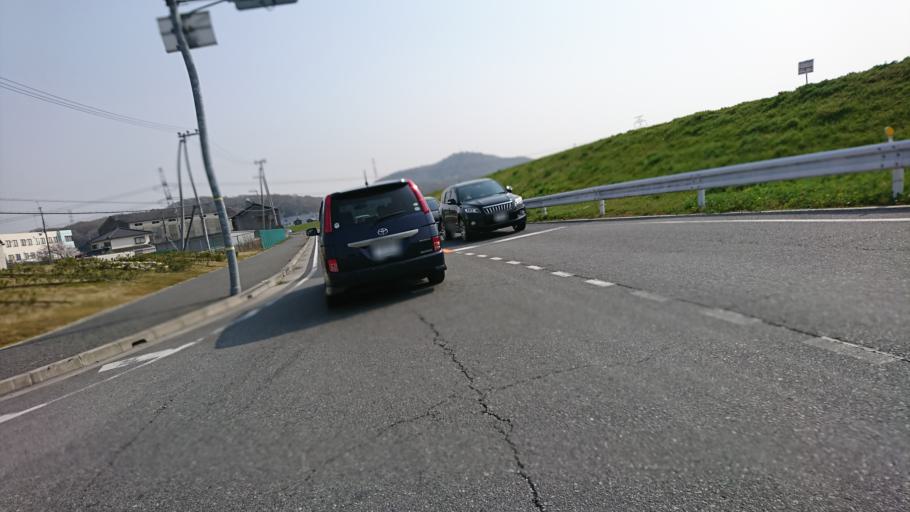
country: JP
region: Hyogo
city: Ono
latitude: 34.8223
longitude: 134.9377
